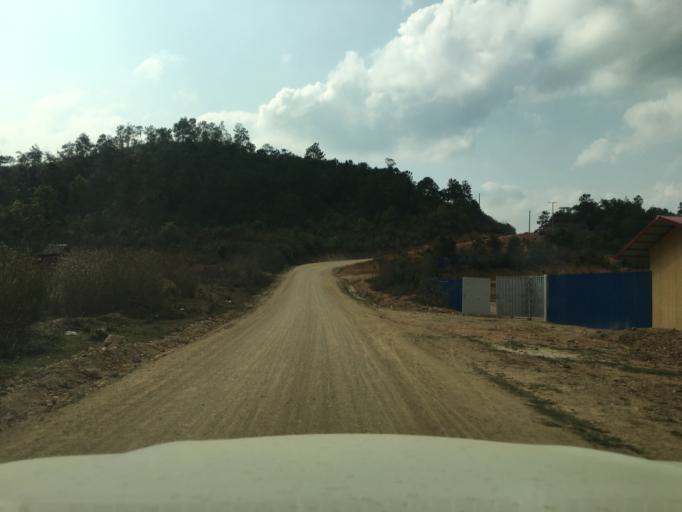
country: LA
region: Houaphan
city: Huameung
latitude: 20.2090
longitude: 103.8731
